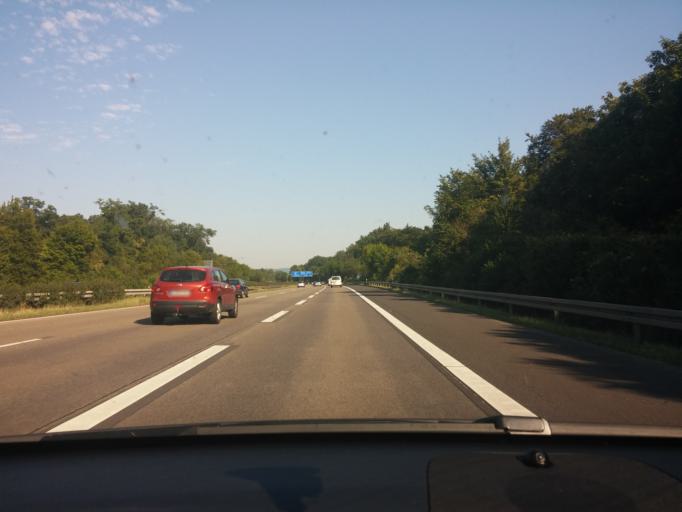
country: DE
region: Hesse
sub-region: Regierungsbezirk Darmstadt
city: Erlensee
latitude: 50.1408
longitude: 8.9670
